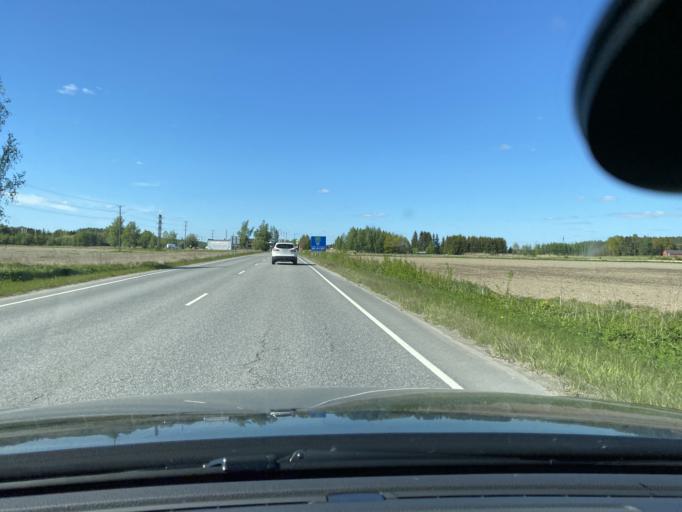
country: FI
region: Varsinais-Suomi
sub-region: Turku
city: Paimio
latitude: 60.4166
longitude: 22.6637
